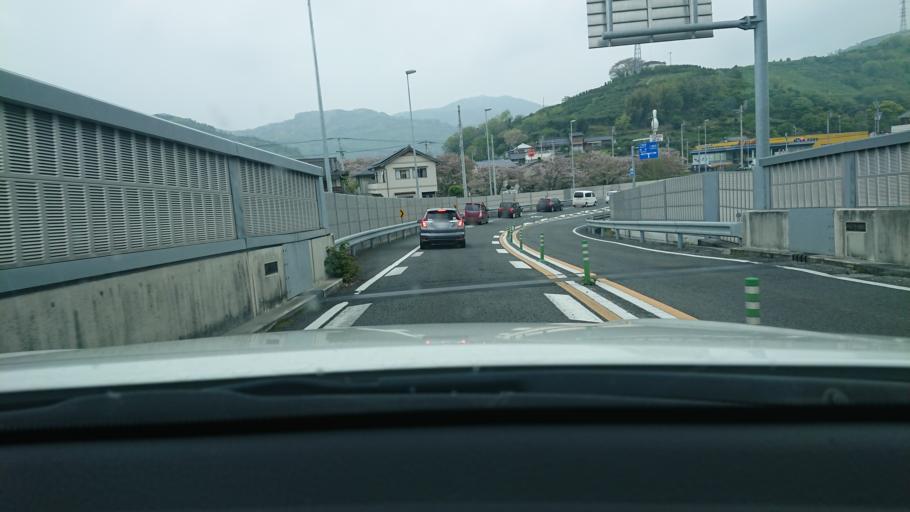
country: JP
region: Ehime
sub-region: Nishiuwa-gun
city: Ikata-cho
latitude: 33.4822
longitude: 132.4052
